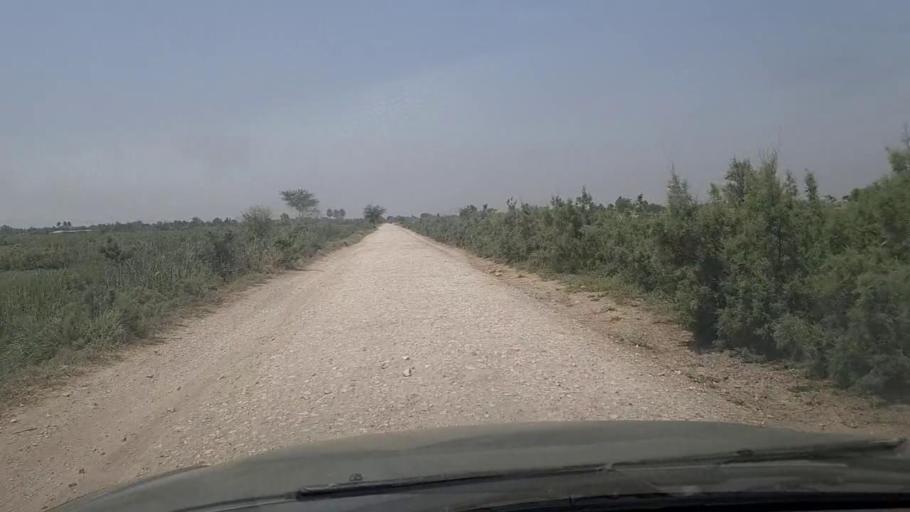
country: PK
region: Sindh
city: Adilpur
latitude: 27.9361
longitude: 69.2830
